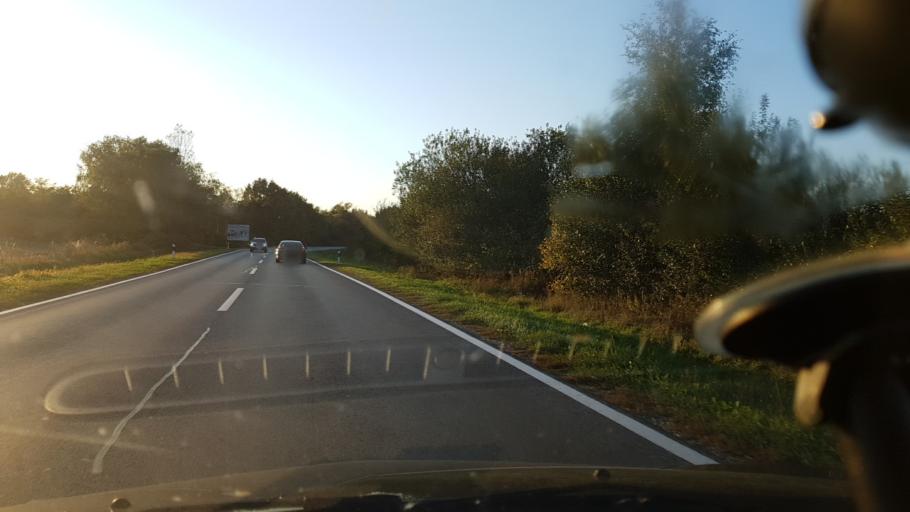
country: HR
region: Koprivnicko-Krizevacka
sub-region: Grad Koprivnica
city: Koprivnica
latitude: 46.1451
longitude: 16.8240
